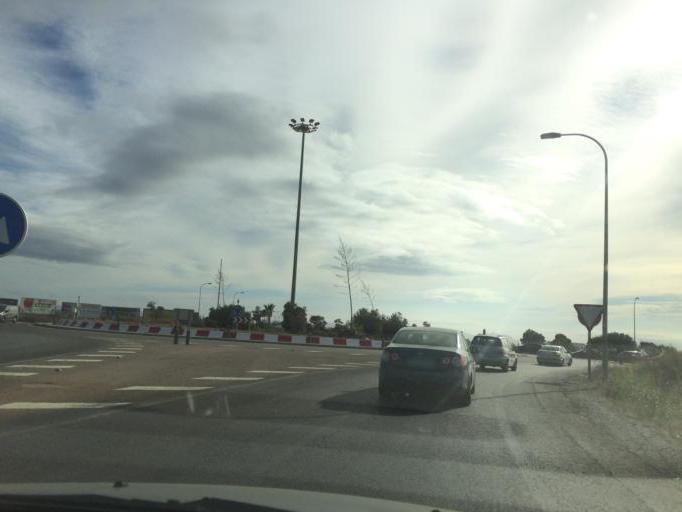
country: ES
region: Andalusia
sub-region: Provincia de Almeria
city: Retamar
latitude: 36.8553
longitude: -2.3457
